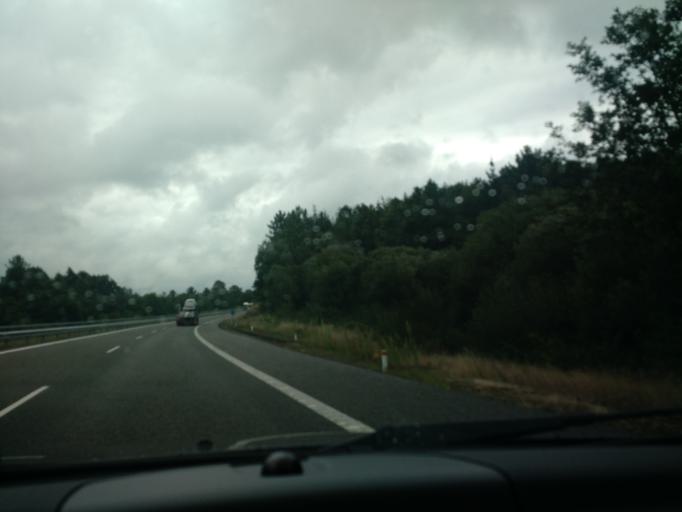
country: ES
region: Galicia
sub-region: Provincia da Coruna
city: Oroso
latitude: 42.9252
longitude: -8.4776
